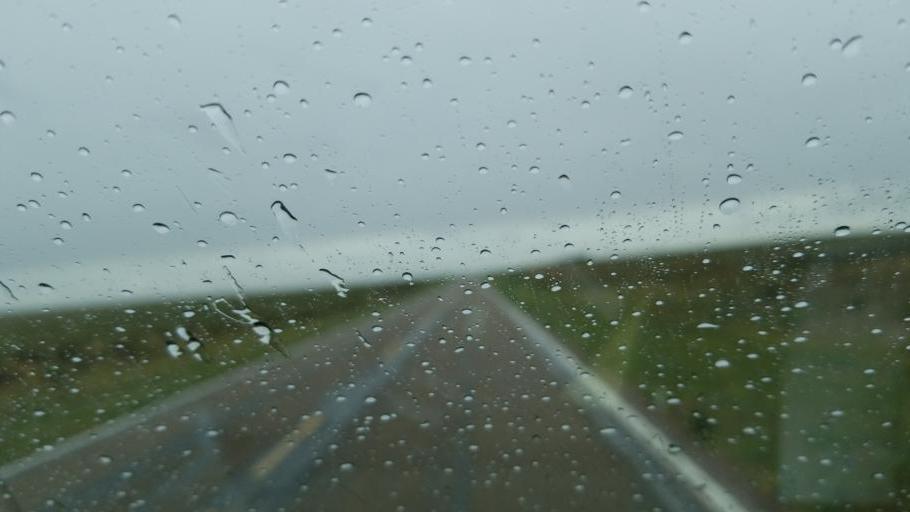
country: US
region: Colorado
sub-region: Lincoln County
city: Hugo
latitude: 38.8496
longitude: -103.1771
